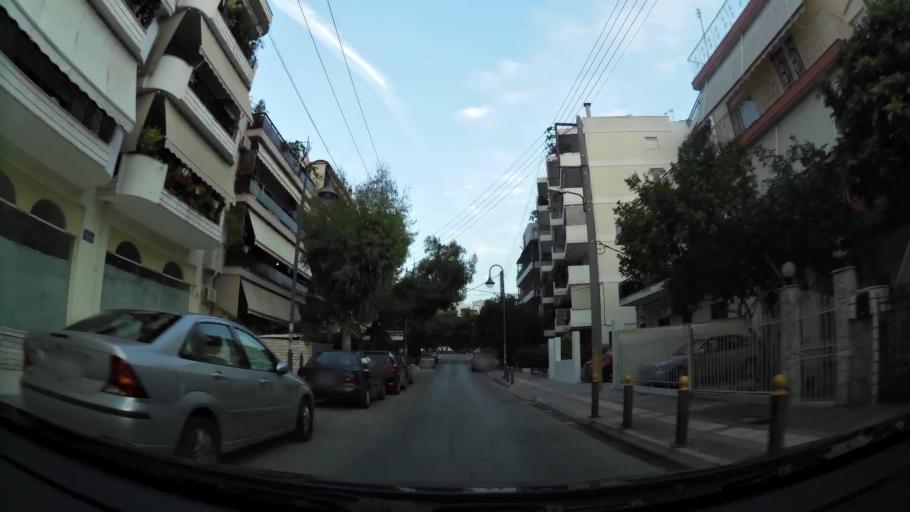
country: GR
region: Attica
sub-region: Nomarchia Athinas
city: Moskhaton
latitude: 37.9523
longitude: 23.6868
